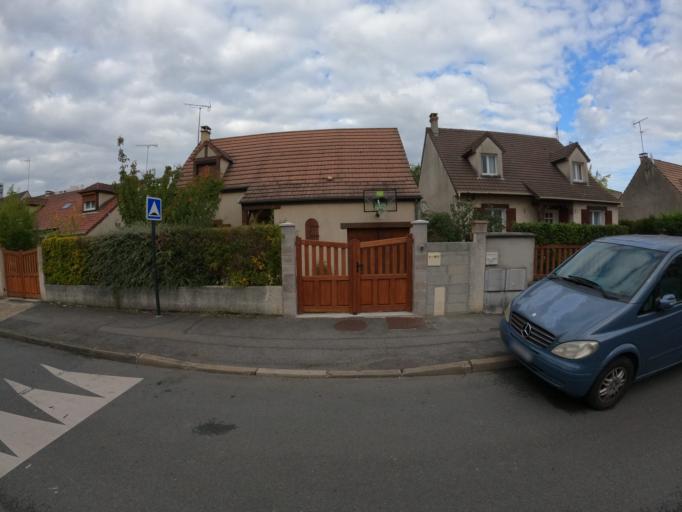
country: FR
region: Ile-de-France
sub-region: Departement de Seine-et-Marne
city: Chelles
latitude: 48.8834
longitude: 2.5844
